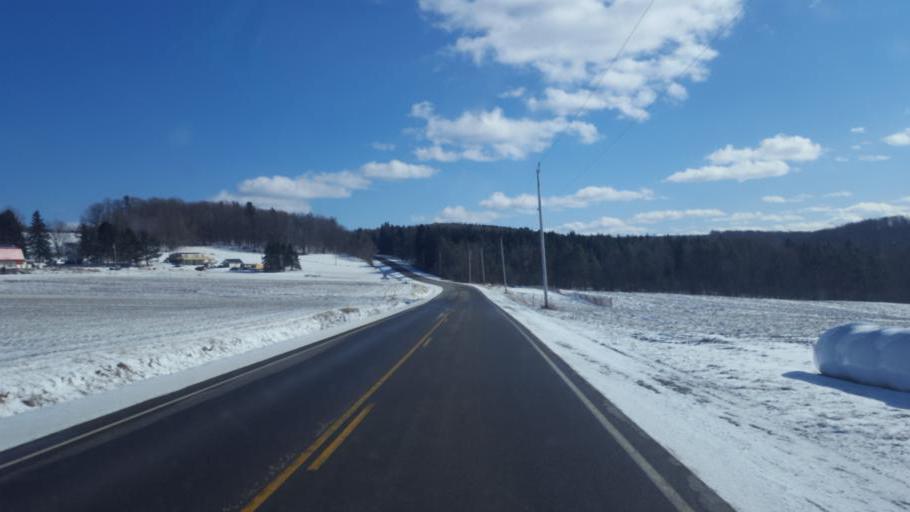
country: US
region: New York
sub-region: Allegany County
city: Friendship
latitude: 42.1912
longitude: -78.0920
